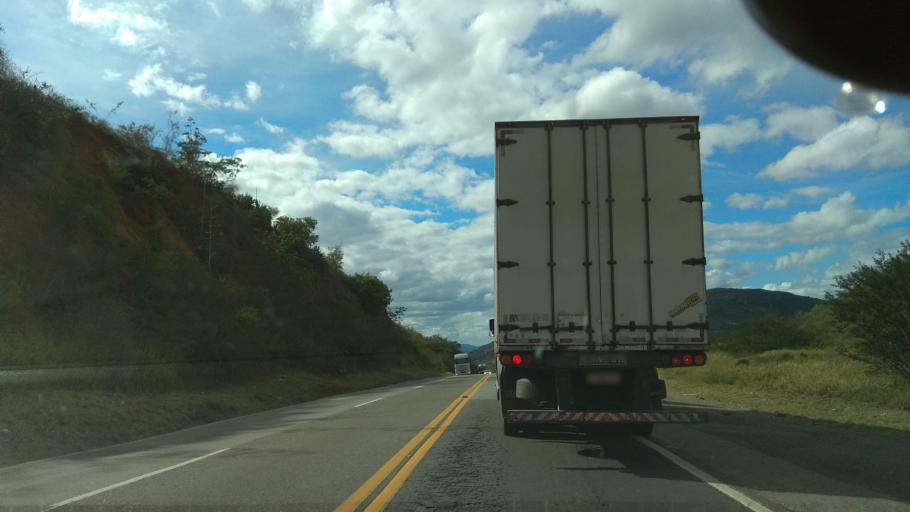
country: BR
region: Bahia
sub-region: Amargosa
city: Amargosa
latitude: -12.8946
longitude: -39.8604
